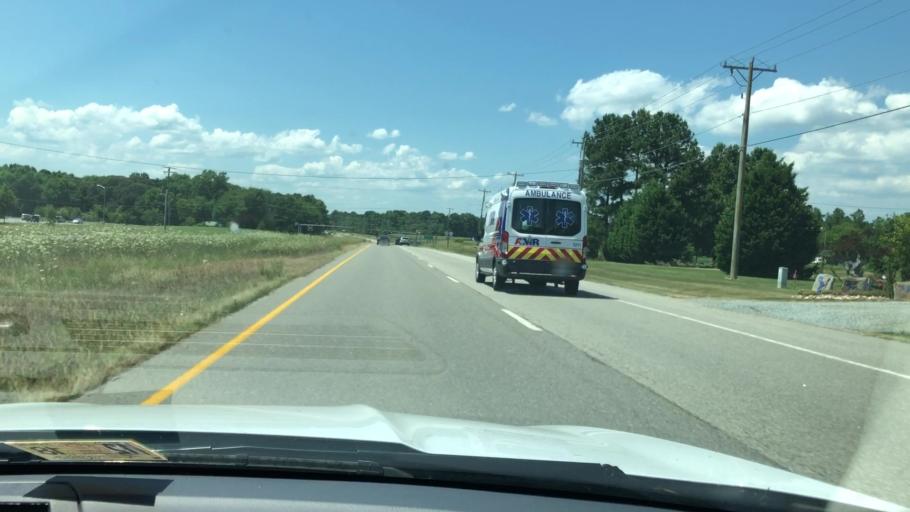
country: US
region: Virginia
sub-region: Middlesex County
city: Saluda
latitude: 37.5909
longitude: -76.4953
